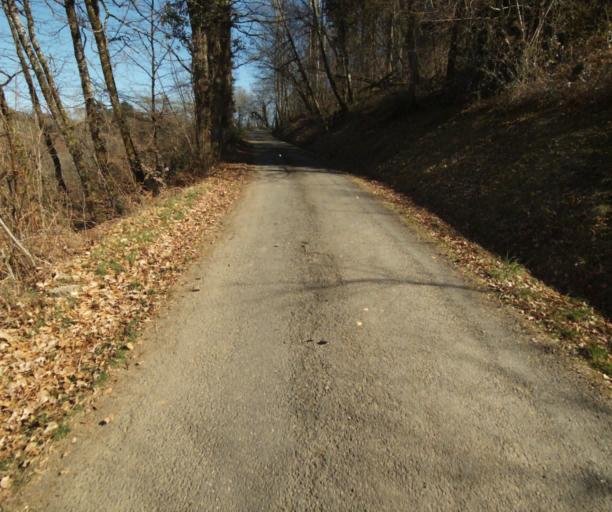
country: FR
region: Limousin
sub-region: Departement de la Correze
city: Chamboulive
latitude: 45.4176
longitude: 1.6473
